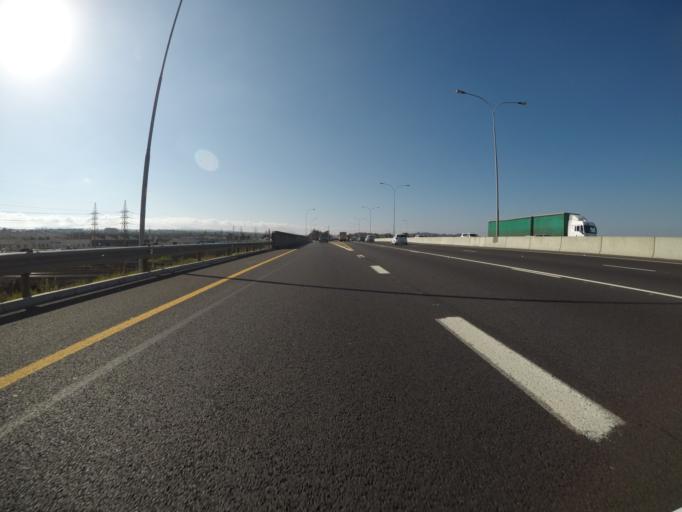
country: ZA
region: Western Cape
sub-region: City of Cape Town
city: Kraaifontein
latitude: -33.8909
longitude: 18.6765
